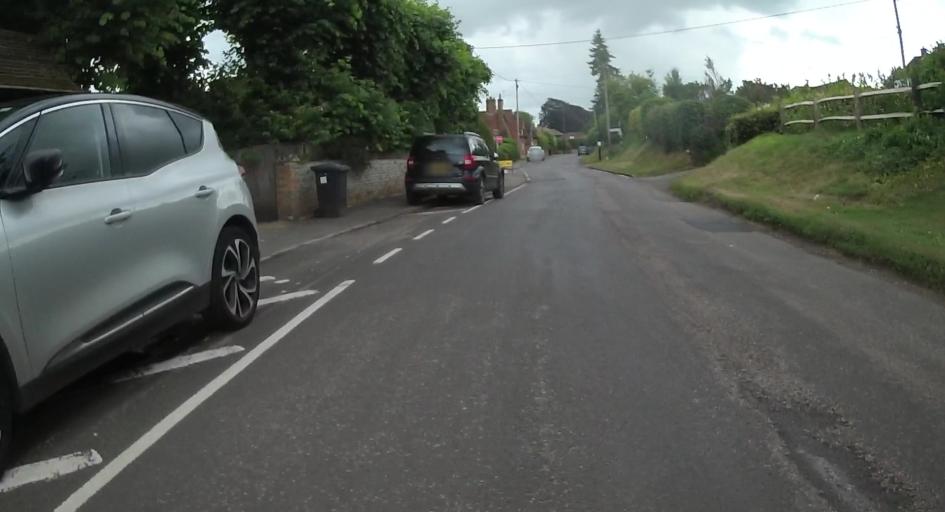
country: GB
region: England
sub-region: Hampshire
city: Fleet
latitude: 51.2305
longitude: -0.8579
